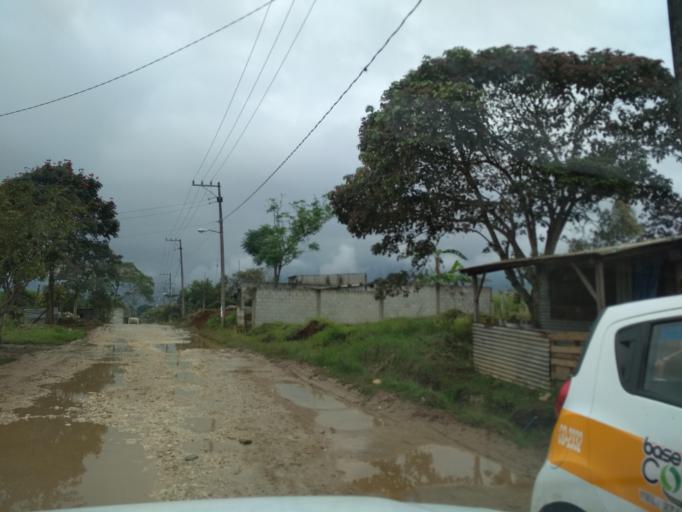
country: MX
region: Veracruz
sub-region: Cordoba
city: San Jose de Tapia
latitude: 18.8450
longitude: -96.9672
